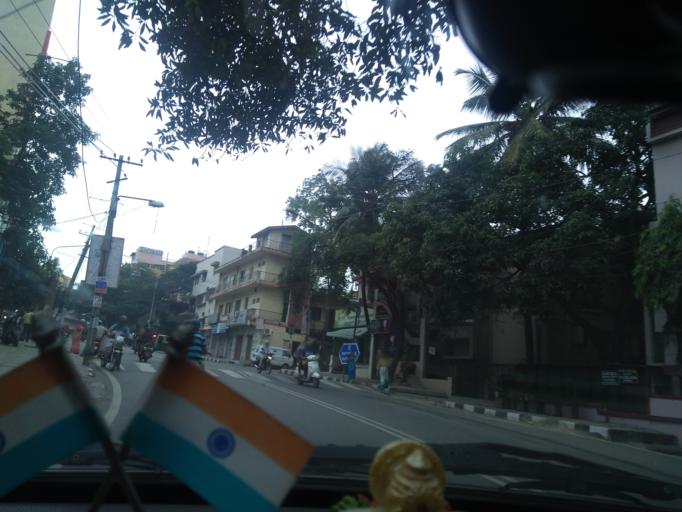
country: IN
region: Karnataka
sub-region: Bangalore Urban
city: Bangalore
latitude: 12.9860
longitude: 77.5512
